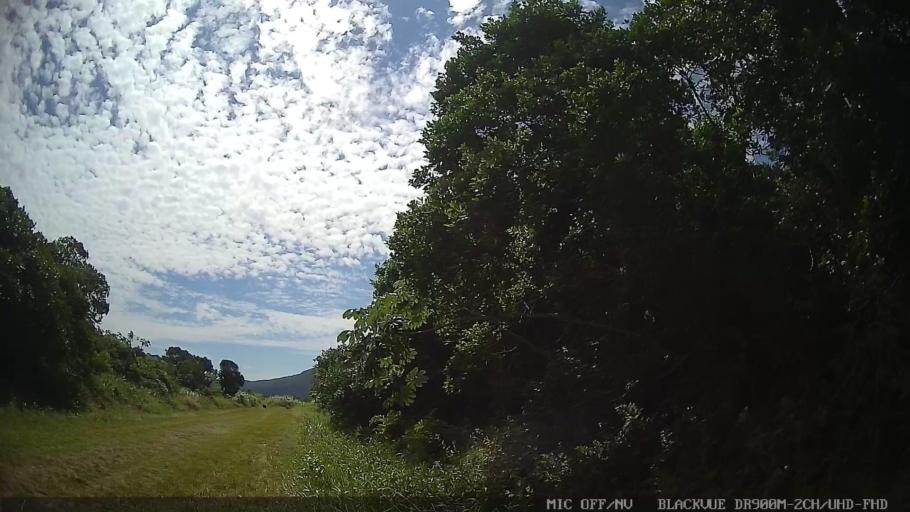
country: BR
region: Sao Paulo
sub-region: Iguape
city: Iguape
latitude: -24.7160
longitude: -47.5046
